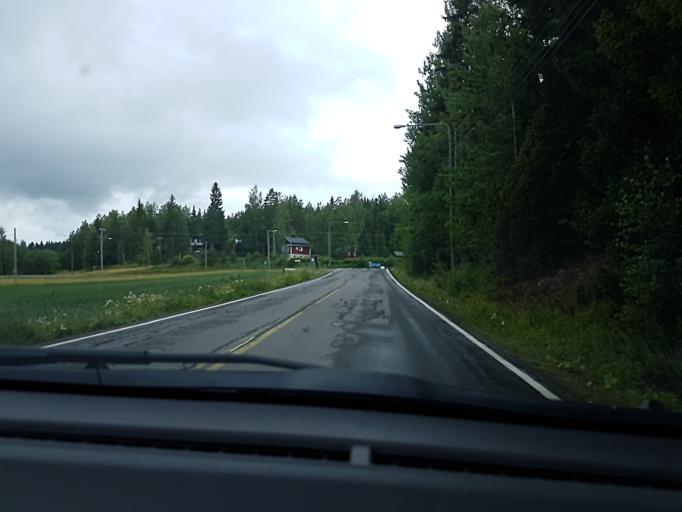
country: FI
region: Uusimaa
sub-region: Helsinki
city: Pornainen
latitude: 60.4395
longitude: 25.3787
